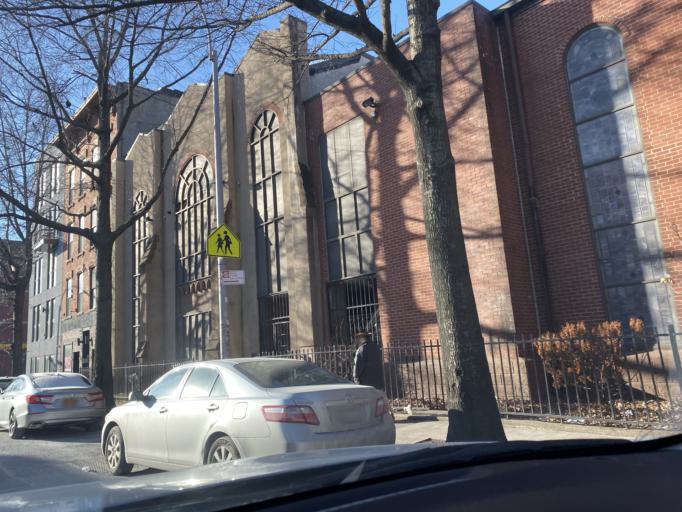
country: US
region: New York
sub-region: Kings County
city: Brooklyn
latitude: 40.6876
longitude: -73.9300
